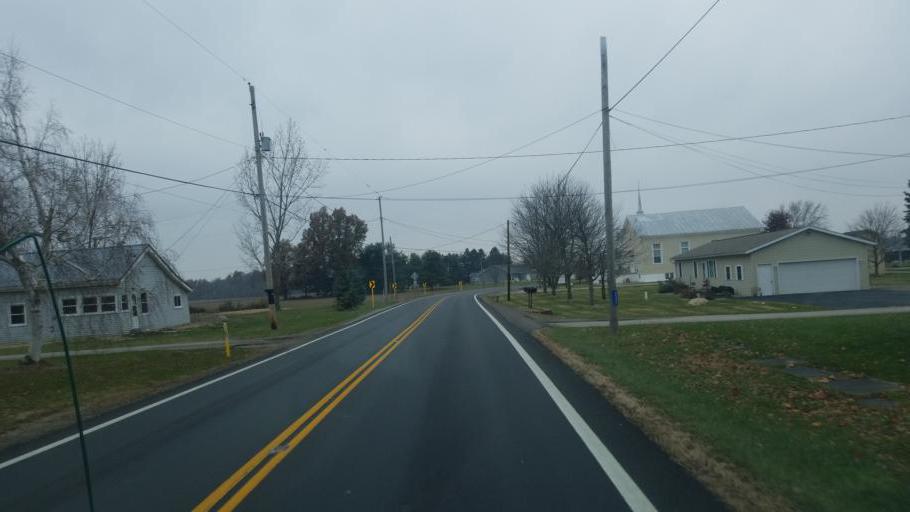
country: US
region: Ohio
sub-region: Crawford County
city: Crestline
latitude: 40.7961
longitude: -82.7887
